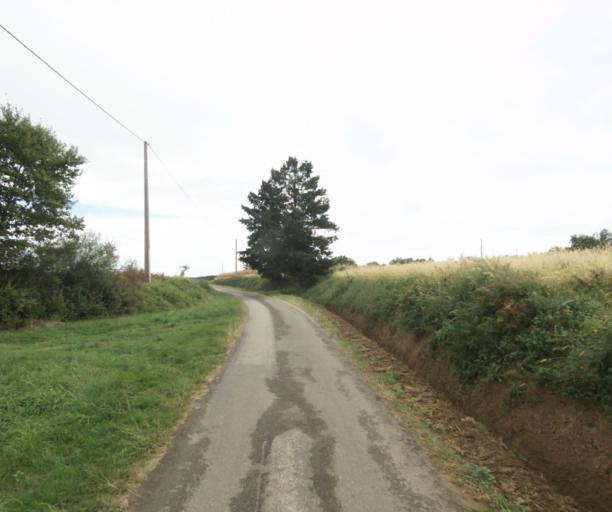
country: FR
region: Midi-Pyrenees
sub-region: Departement du Gers
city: Cazaubon
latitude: 43.9093
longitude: -0.1542
